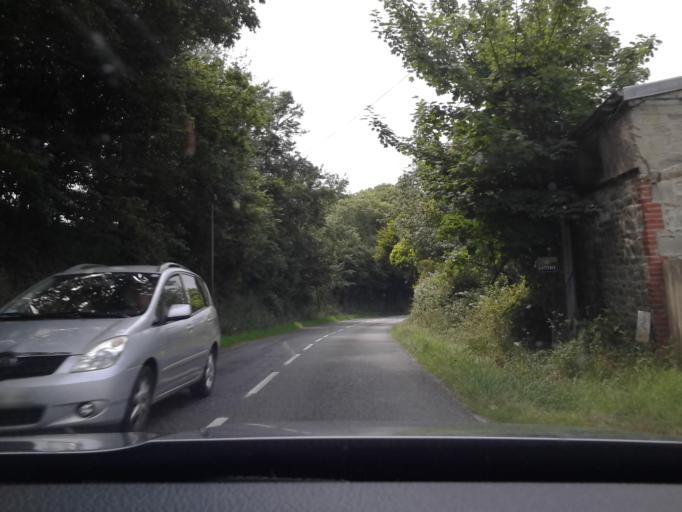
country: FR
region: Lower Normandy
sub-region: Departement de la Manche
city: Beaumont-Hague
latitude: 49.6705
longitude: -1.8207
